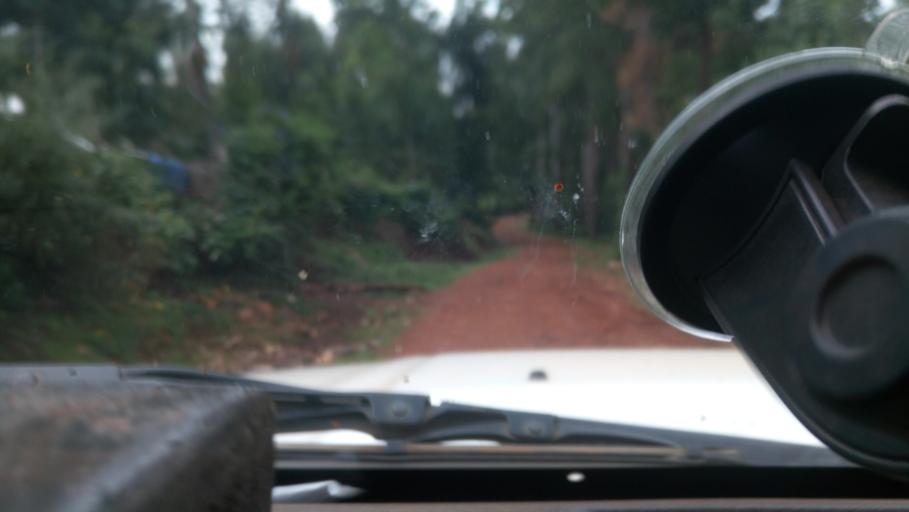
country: KE
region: Kisii
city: Ogembo
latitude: -0.9048
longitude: 34.7777
